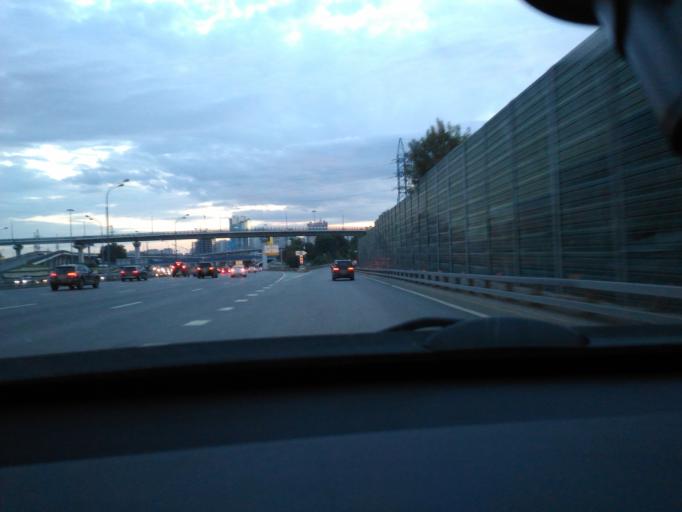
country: RU
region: Moscow
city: Khimki
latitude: 55.8828
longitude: 37.4511
